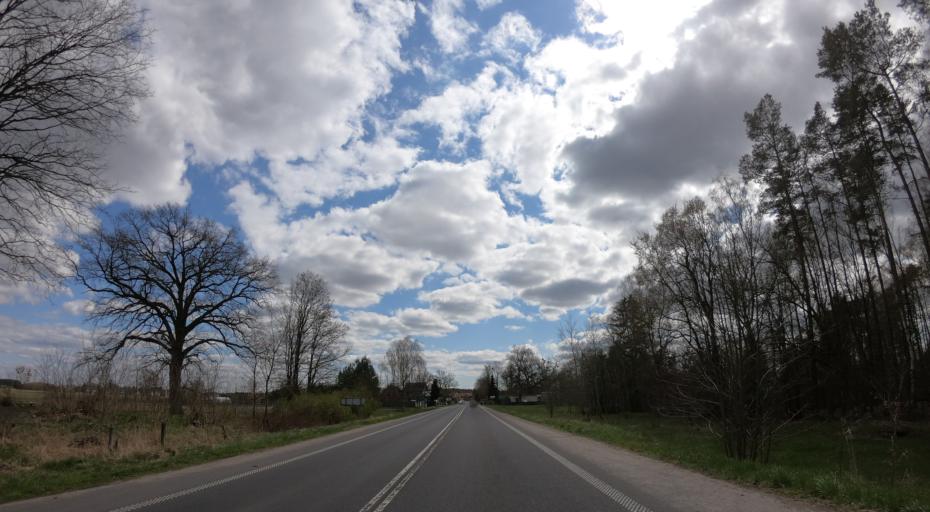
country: PL
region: West Pomeranian Voivodeship
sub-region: Powiat goleniowski
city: Goleniow
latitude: 53.6193
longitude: 14.8195
